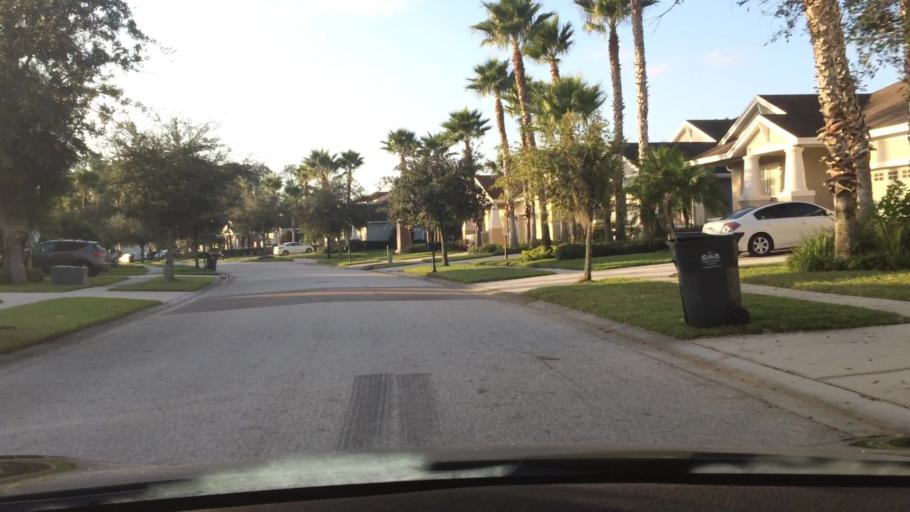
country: US
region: Florida
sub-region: Hillsborough County
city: Pebble Creek
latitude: 28.1630
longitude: -82.3850
